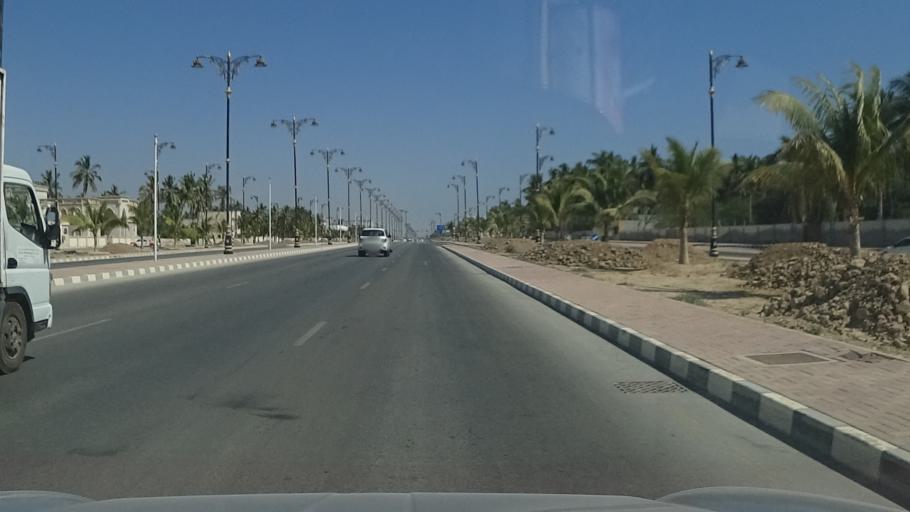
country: OM
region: Zufar
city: Salalah
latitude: 17.0361
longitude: 54.1549
